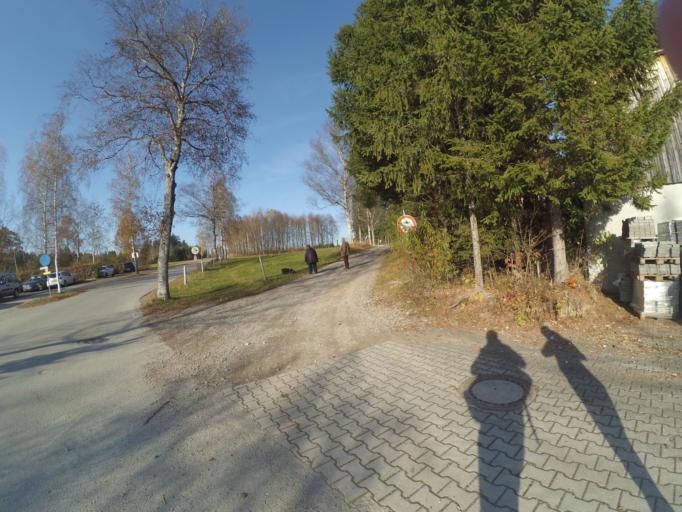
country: DE
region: Bavaria
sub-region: Swabia
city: Aitrang
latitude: 47.8034
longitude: 10.5505
